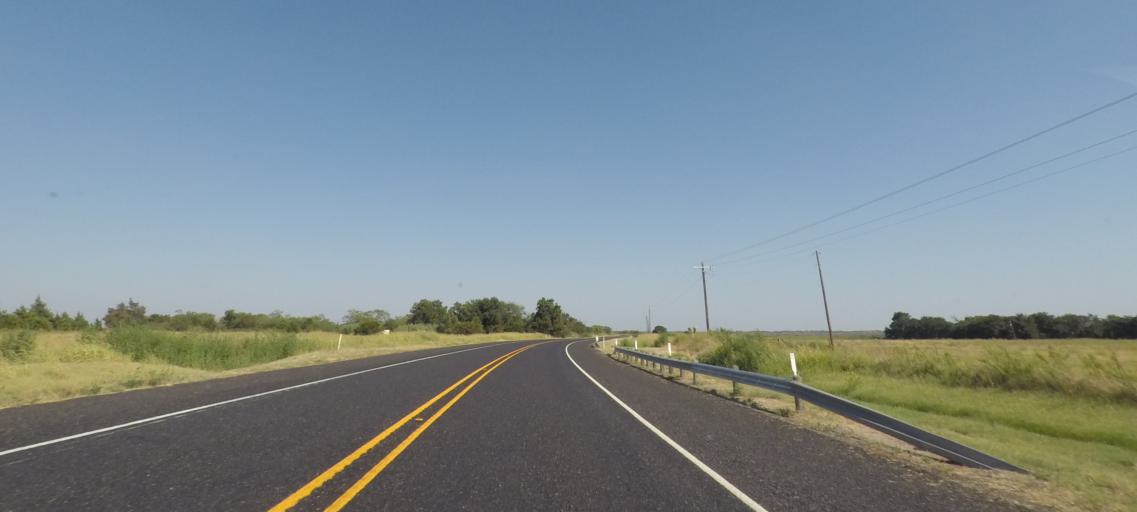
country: US
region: Texas
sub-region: Baylor County
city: Seymour
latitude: 33.6010
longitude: -99.3269
